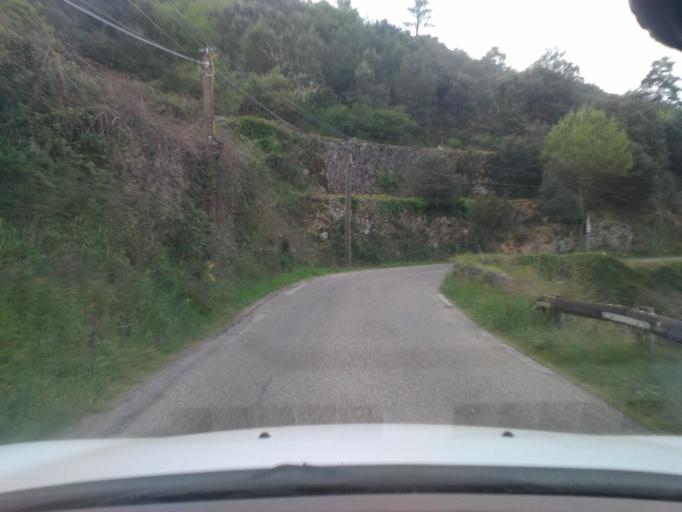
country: FR
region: Languedoc-Roussillon
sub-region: Departement du Gard
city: Lasalle
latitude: 44.0586
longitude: 3.8380
